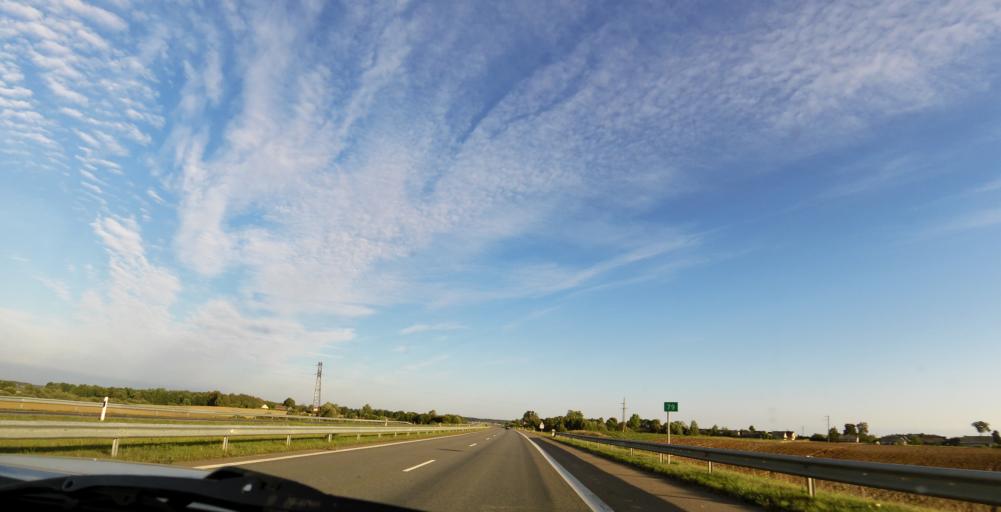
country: LT
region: Vilnius County
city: Ukmerge
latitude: 55.3068
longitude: 24.7909
